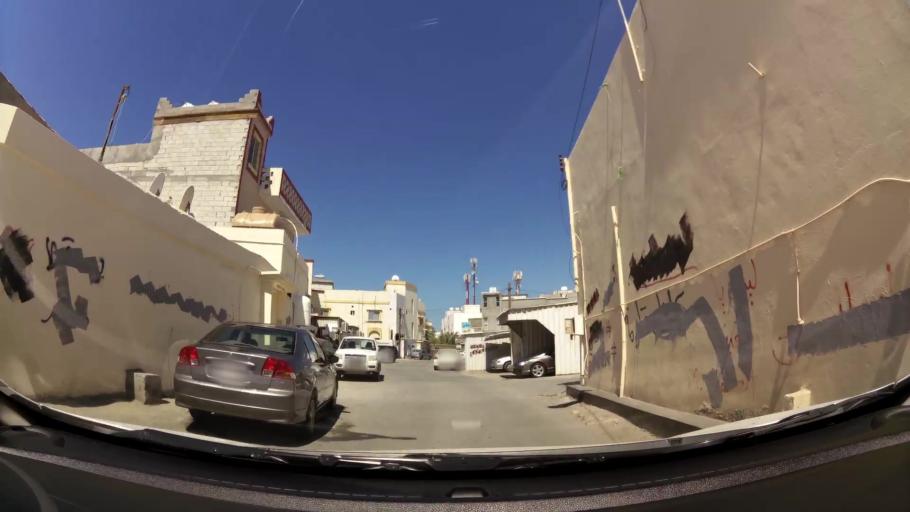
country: BH
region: Muharraq
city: Al Muharraq
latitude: 26.2833
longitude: 50.6240
